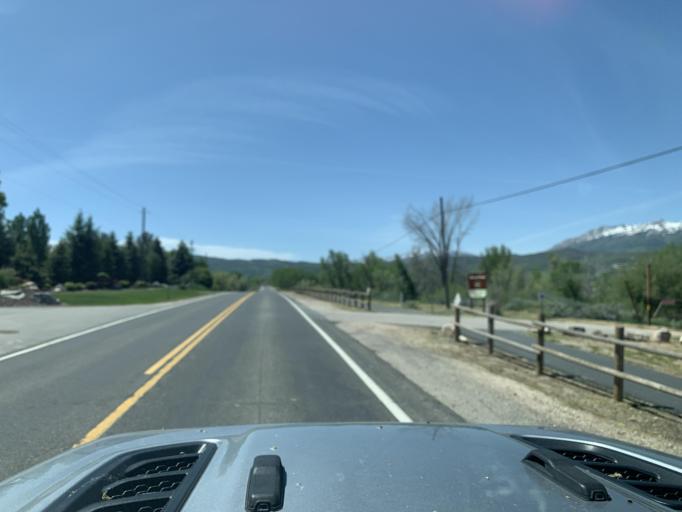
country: US
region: Utah
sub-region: Weber County
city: Wolf Creek
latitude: 41.2776
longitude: -111.7772
